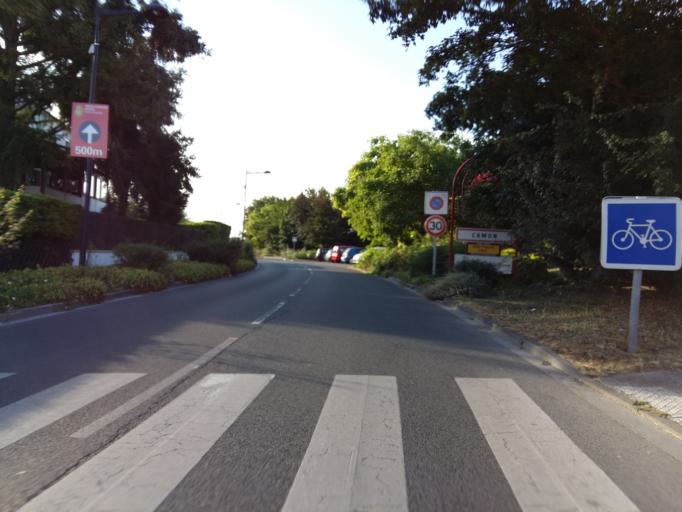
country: FR
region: Picardie
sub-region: Departement de la Somme
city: Rivery
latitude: 49.8966
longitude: 2.3335
